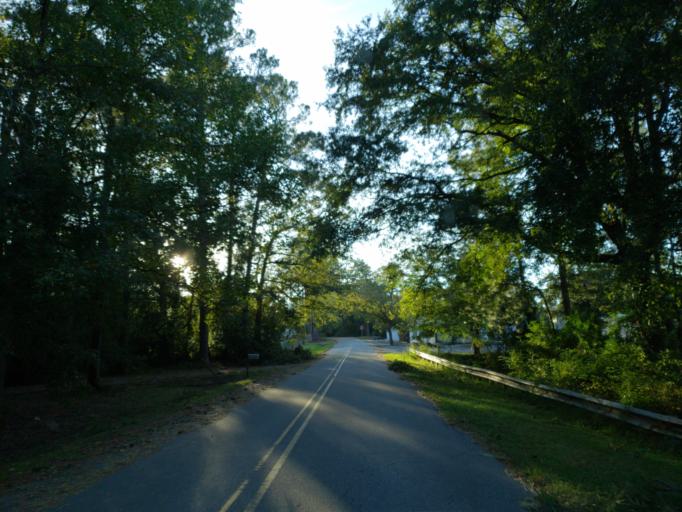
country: US
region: Georgia
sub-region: Tift County
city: Tifton
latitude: 31.4713
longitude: -83.5172
